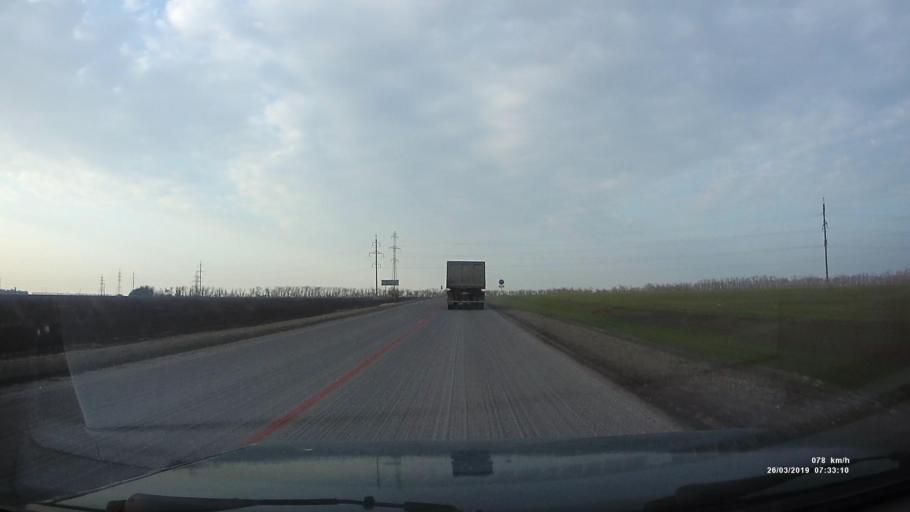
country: RU
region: Rostov
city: Novobessergenovka
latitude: 47.2185
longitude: 38.7719
